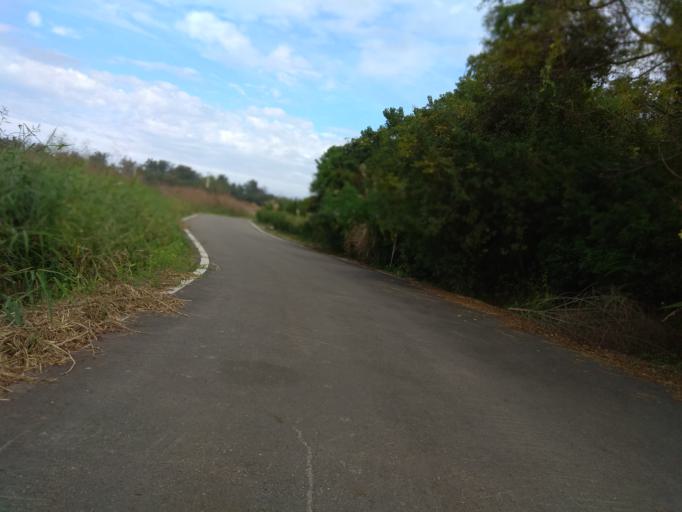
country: TW
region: Taiwan
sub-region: Hsinchu
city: Zhubei
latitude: 24.9597
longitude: 121.0068
